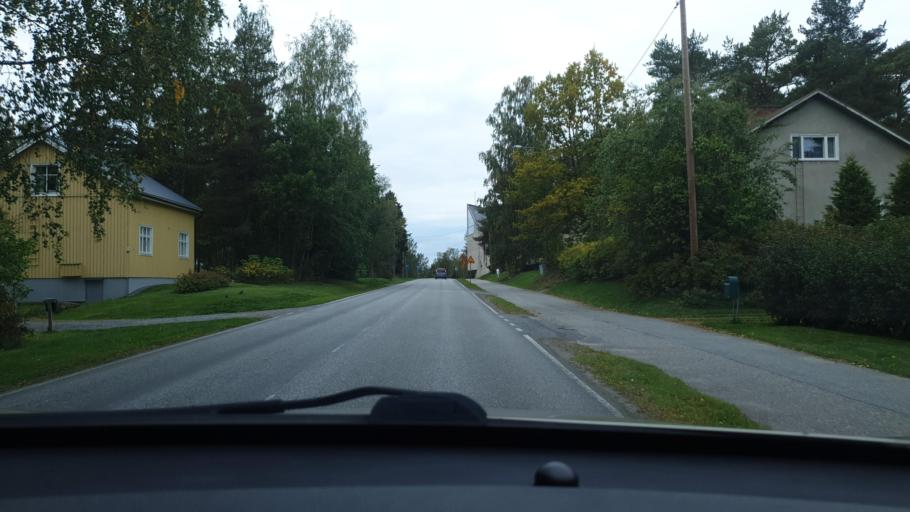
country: FI
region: Ostrobothnia
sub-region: Vaasa
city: Korsholm
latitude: 63.0954
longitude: 21.6661
